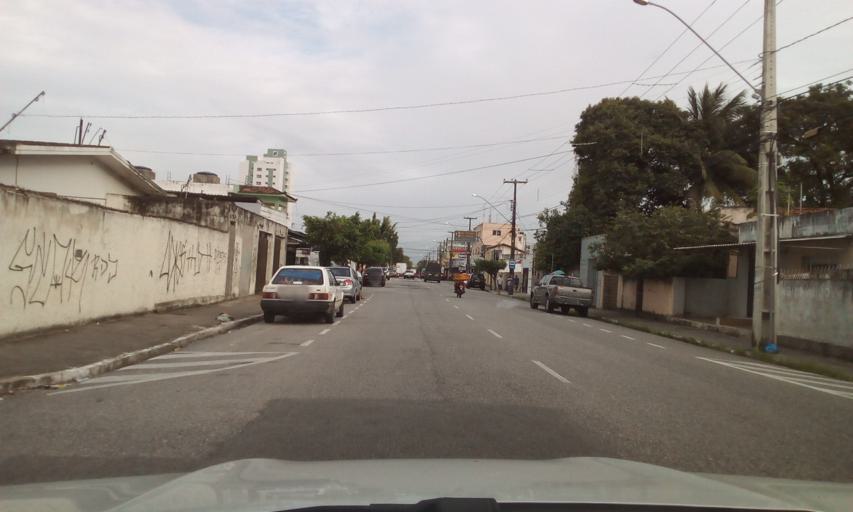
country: BR
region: Paraiba
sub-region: Joao Pessoa
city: Joao Pessoa
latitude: -7.1291
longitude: -34.8807
